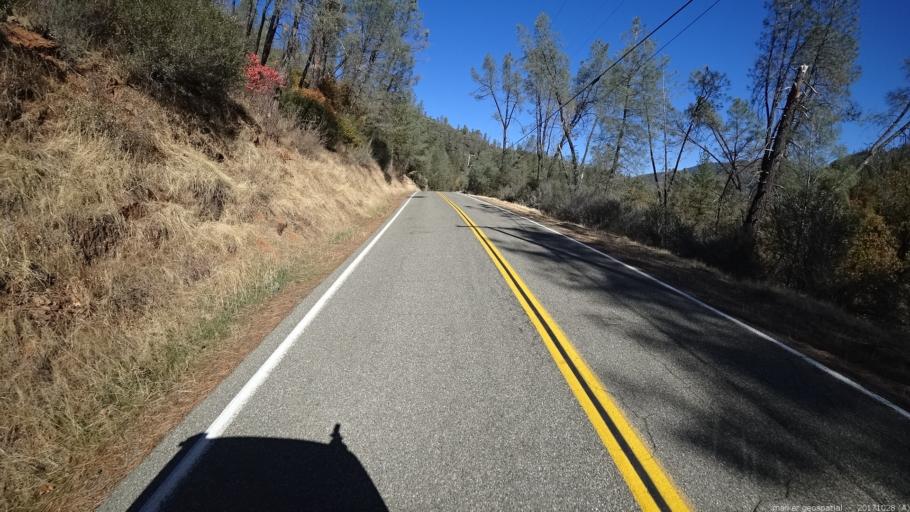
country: US
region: California
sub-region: Trinity County
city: Lewiston
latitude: 40.7433
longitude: -122.6257
